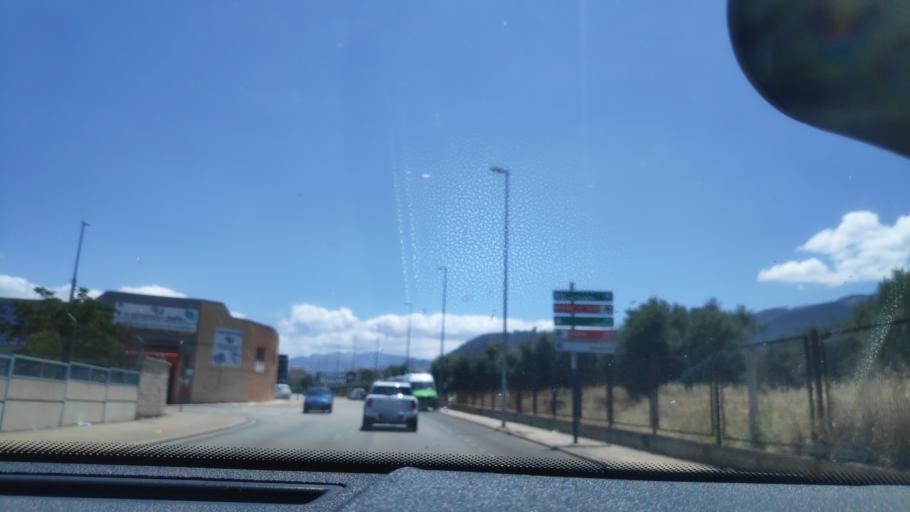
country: ES
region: Andalusia
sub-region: Provincia de Jaen
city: Jaen
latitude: 37.7966
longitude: -3.7930
